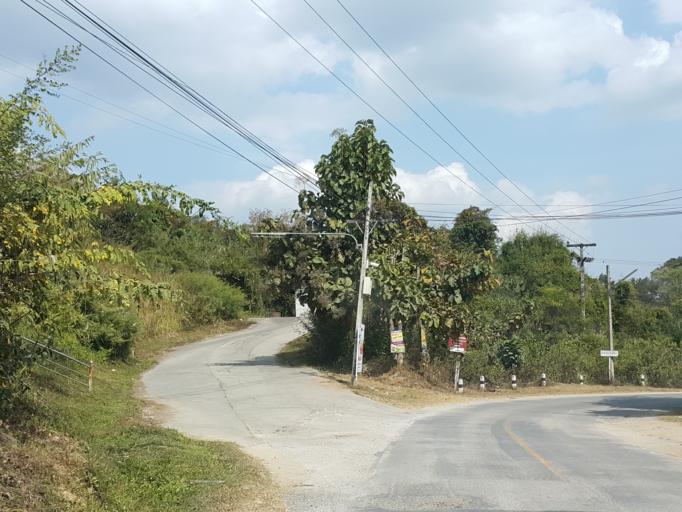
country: TH
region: Chiang Mai
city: Om Koi
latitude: 17.7999
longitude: 98.3635
